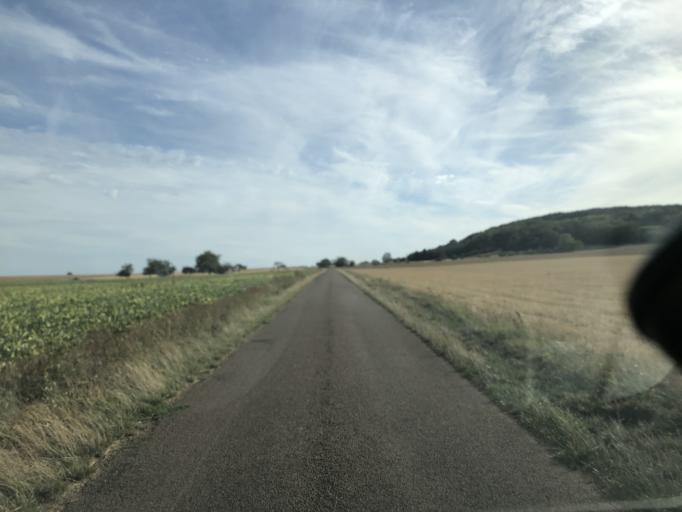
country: FR
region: Bourgogne
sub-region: Departement de l'Yonne
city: Joigny
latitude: 47.9483
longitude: 3.3945
